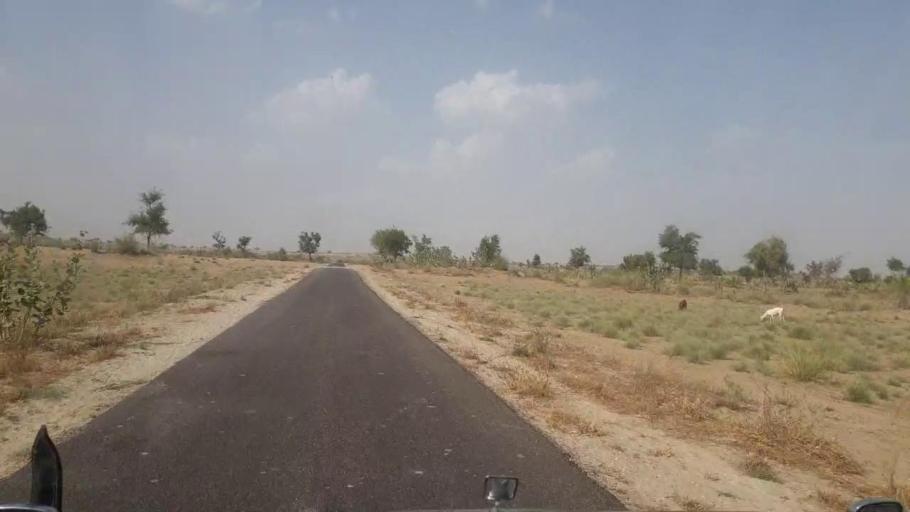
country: PK
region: Sindh
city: Islamkot
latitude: 25.2009
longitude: 70.2838
